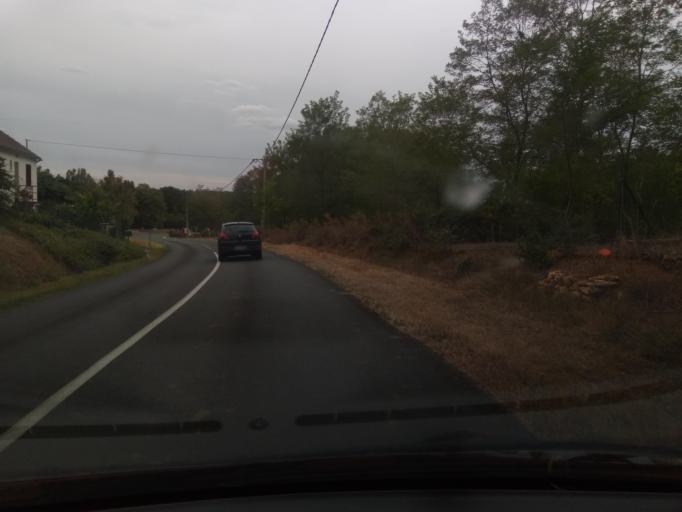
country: FR
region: Poitou-Charentes
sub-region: Departement de la Vienne
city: Pleumartin
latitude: 46.6445
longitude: 0.7581
